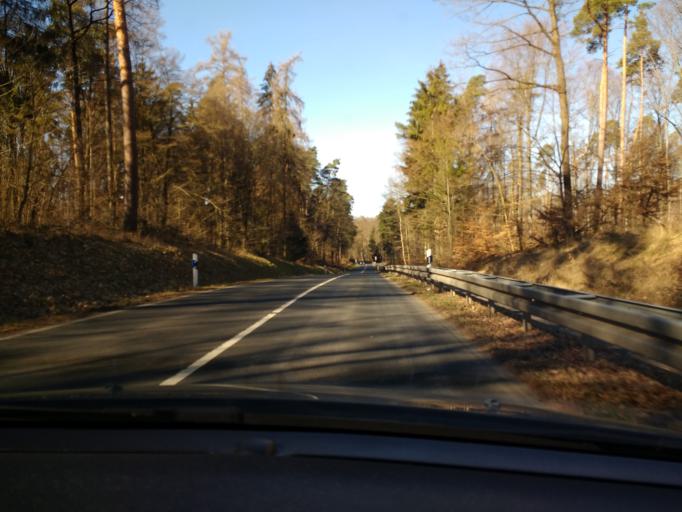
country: DE
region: Bavaria
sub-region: Regierungsbezirk Unterfranken
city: Alzenau in Unterfranken
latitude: 50.1253
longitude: 9.0844
